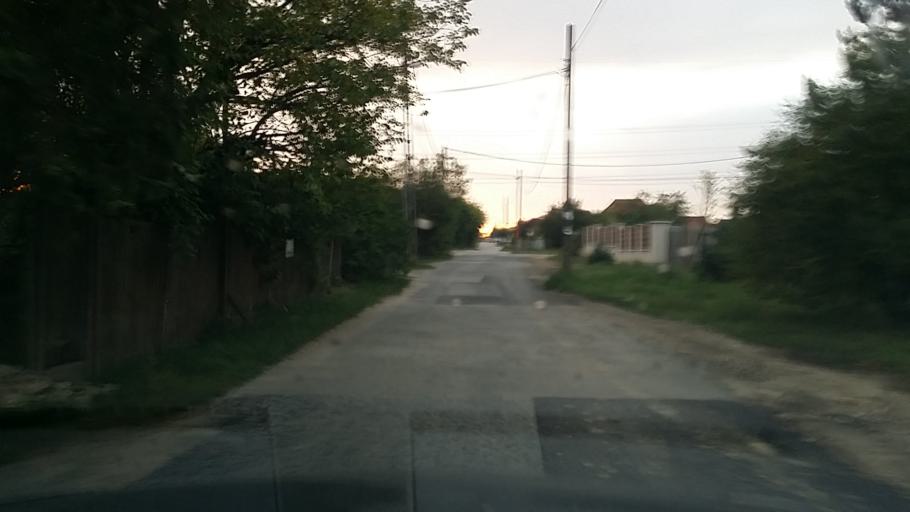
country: HU
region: Pest
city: Urom
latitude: 47.5819
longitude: 19.0165
